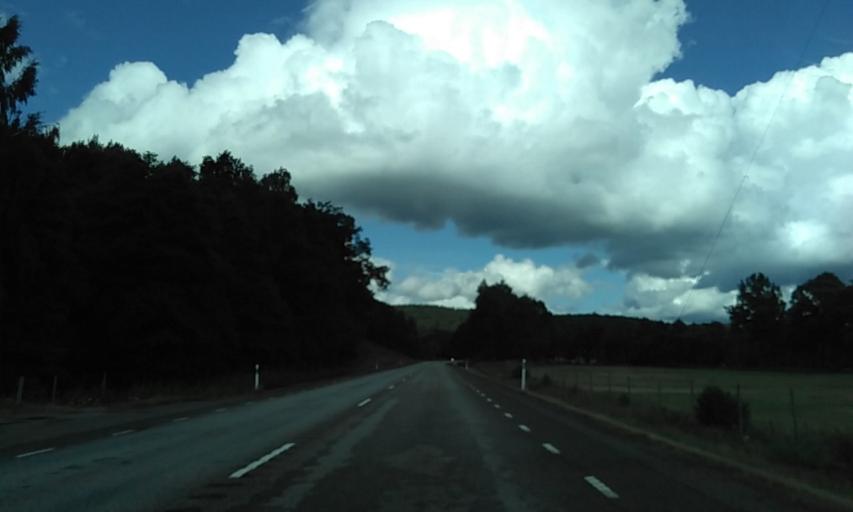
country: SE
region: Vaestra Goetaland
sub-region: Alingsas Kommun
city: Ingared
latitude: 57.9570
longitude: 12.3971
